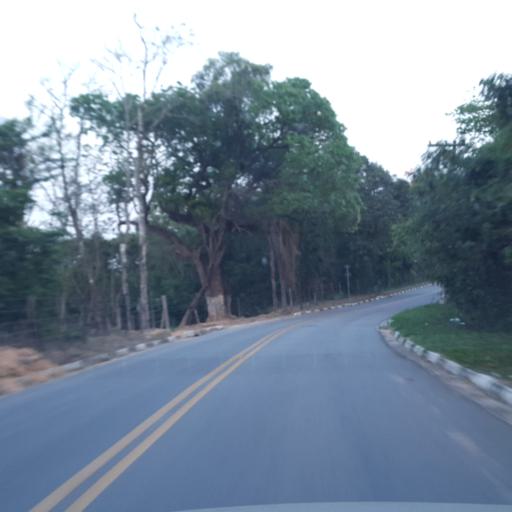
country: BR
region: Sao Paulo
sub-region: Louveira
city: Louveira
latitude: -23.0648
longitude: -46.9634
